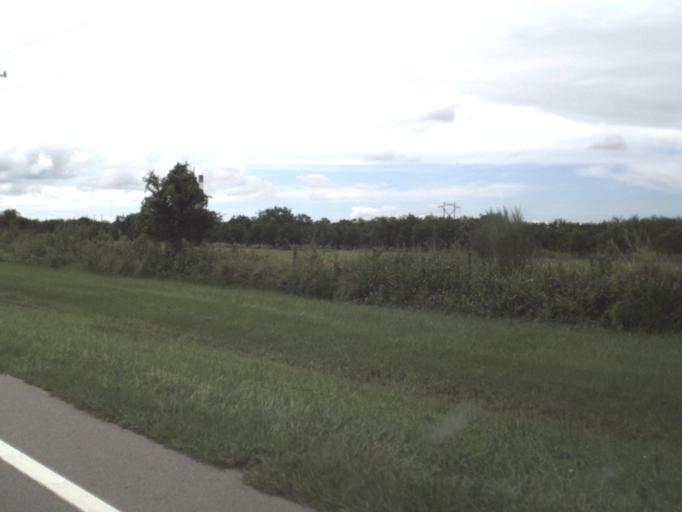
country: US
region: Florida
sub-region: Hillsborough County
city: Wimauma
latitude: 27.6021
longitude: -82.3199
